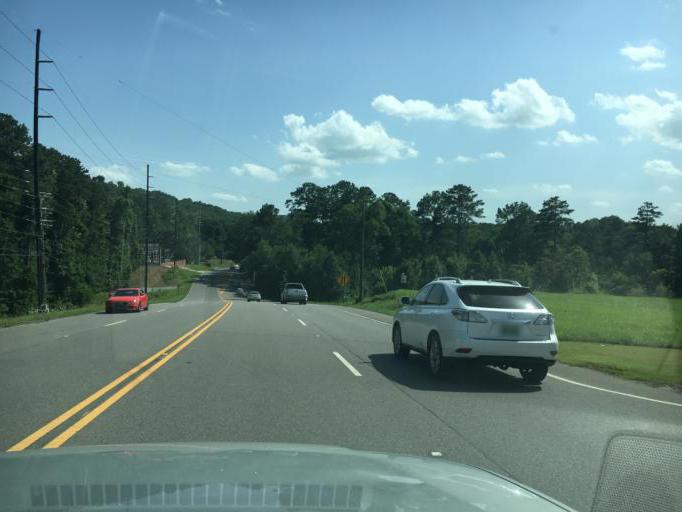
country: US
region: Alabama
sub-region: Shelby County
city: Meadowbrook
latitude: 33.4134
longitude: -86.7005
